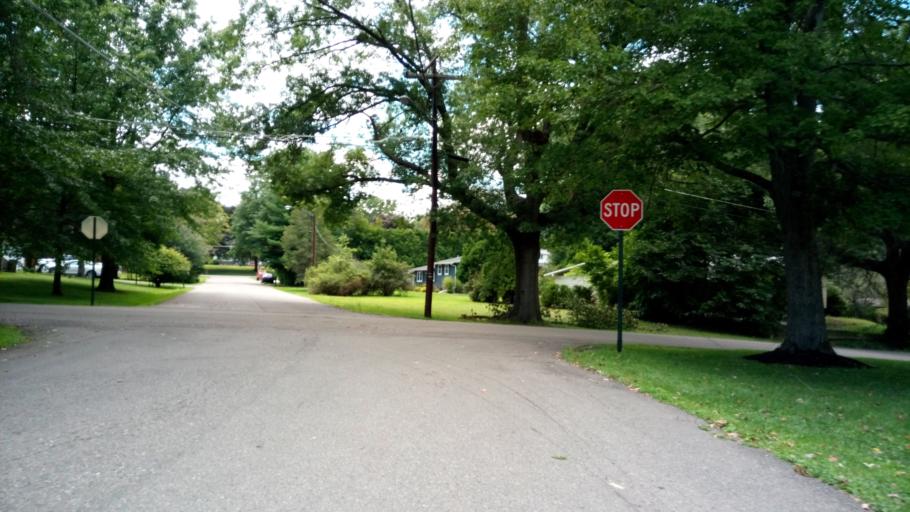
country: US
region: New York
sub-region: Chemung County
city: West Elmira
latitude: 42.0890
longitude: -76.8335
